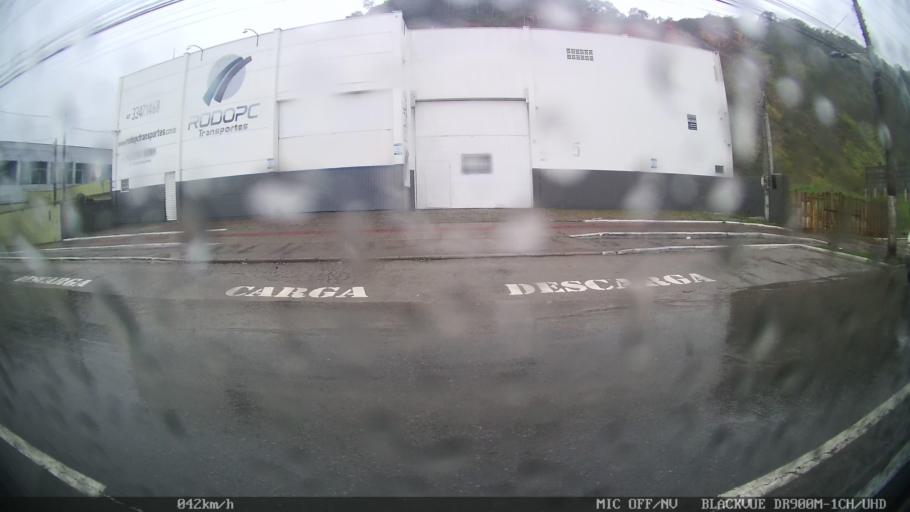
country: BR
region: Santa Catarina
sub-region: Itajai
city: Itajai
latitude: -26.9336
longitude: -48.6907
